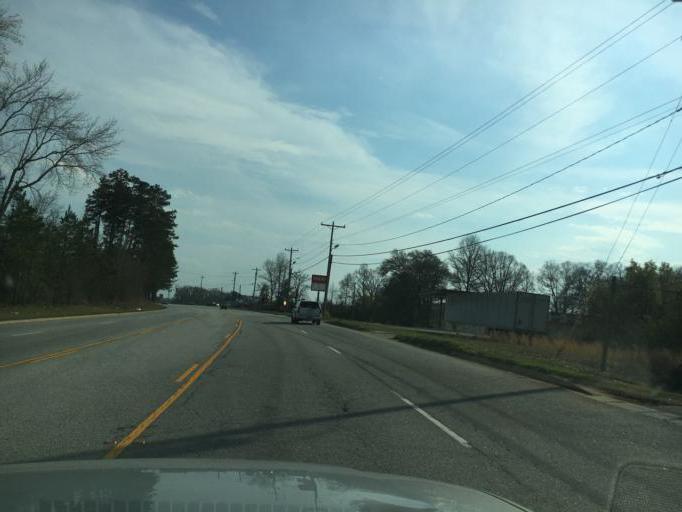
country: US
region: South Carolina
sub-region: Spartanburg County
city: Mayo
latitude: 35.0317
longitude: -81.8963
